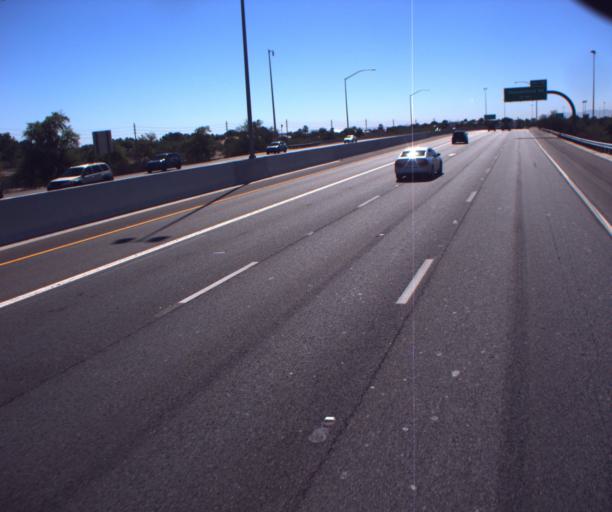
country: US
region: Arizona
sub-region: Maricopa County
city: Sun City
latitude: 33.6231
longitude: -112.2401
